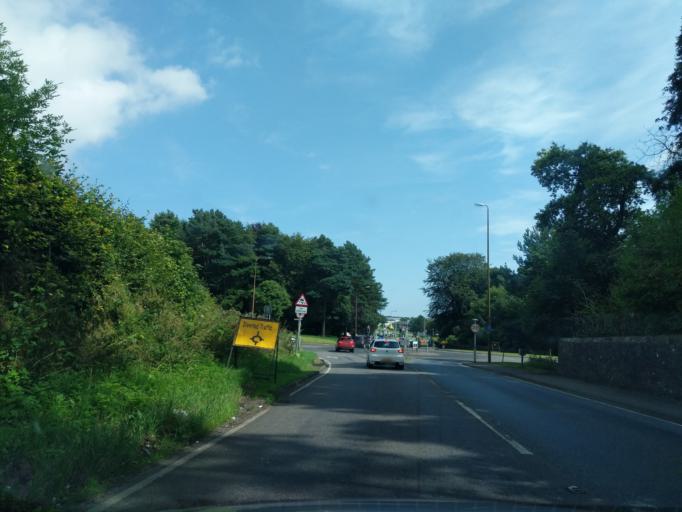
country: GB
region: Scotland
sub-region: Angus
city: Muirhead
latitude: 56.4831
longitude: -3.0219
